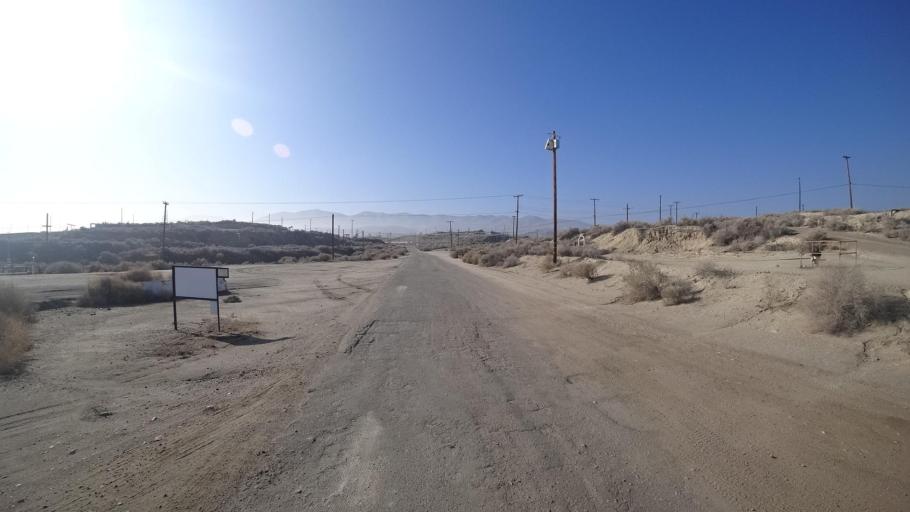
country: US
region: California
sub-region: Kern County
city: Taft Heights
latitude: 35.2218
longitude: -119.5972
